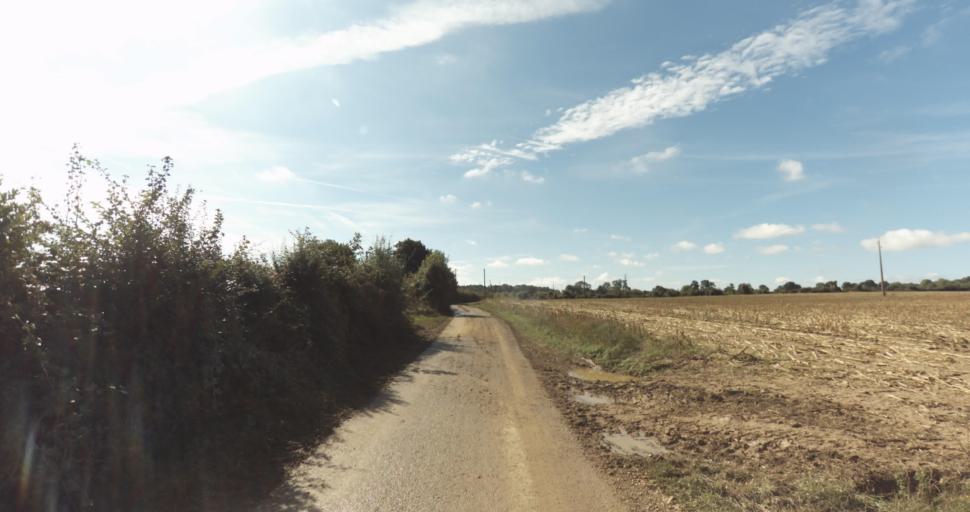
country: FR
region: Lower Normandy
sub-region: Departement du Calvados
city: Orbec
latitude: 48.9338
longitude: 0.3602
